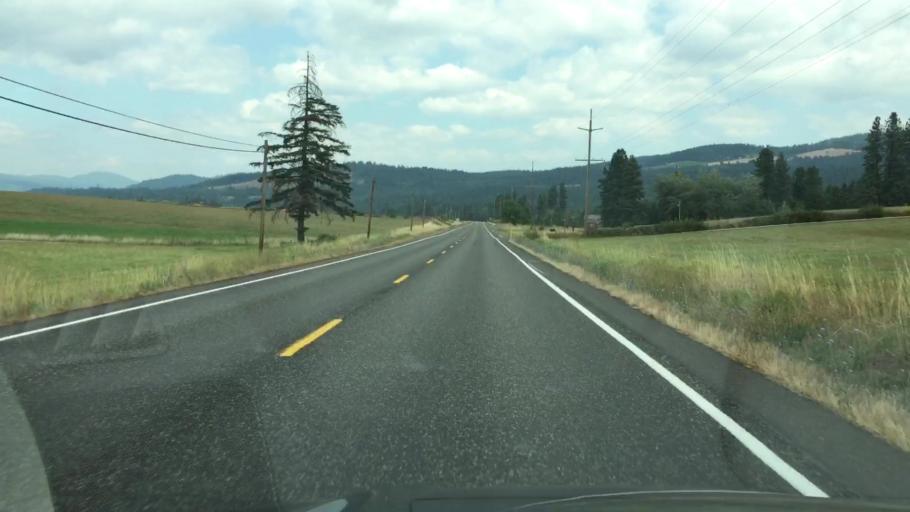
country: US
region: Washington
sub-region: Klickitat County
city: White Salmon
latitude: 45.8127
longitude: -121.4898
